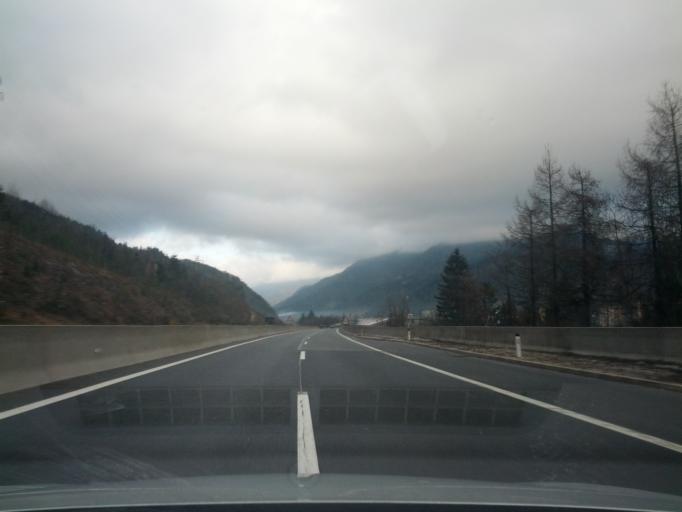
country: SI
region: Jesenice
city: Jesenice
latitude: 46.4297
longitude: 14.0562
